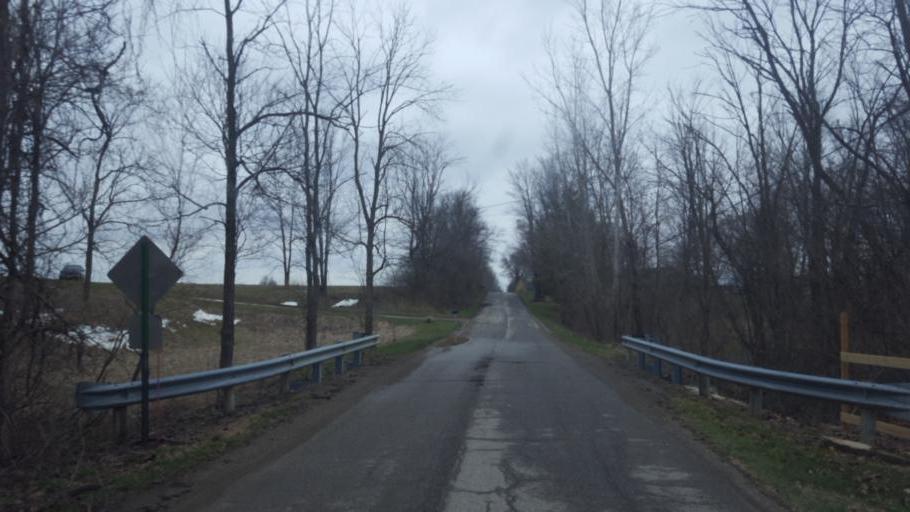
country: US
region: Ohio
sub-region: Delaware County
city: Ashley
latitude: 40.4284
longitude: -83.0111
